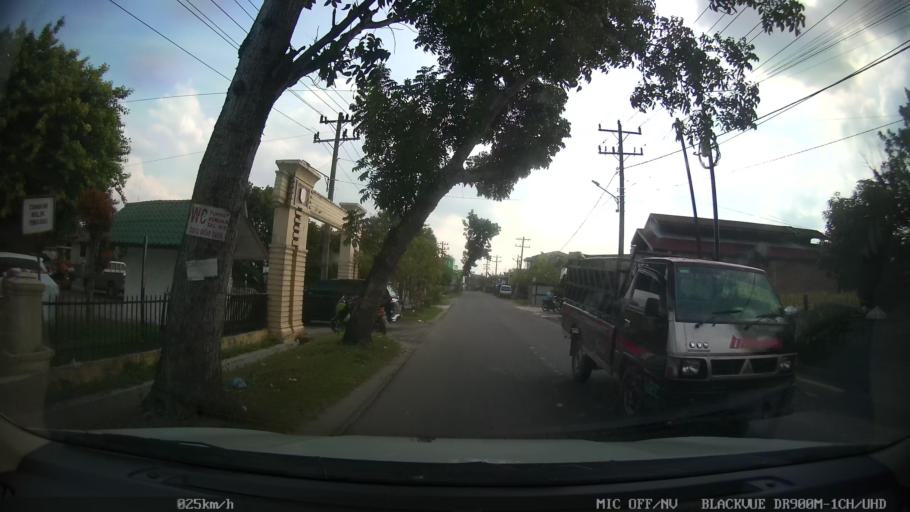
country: ID
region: North Sumatra
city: Binjai
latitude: 3.6378
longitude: 98.4916
